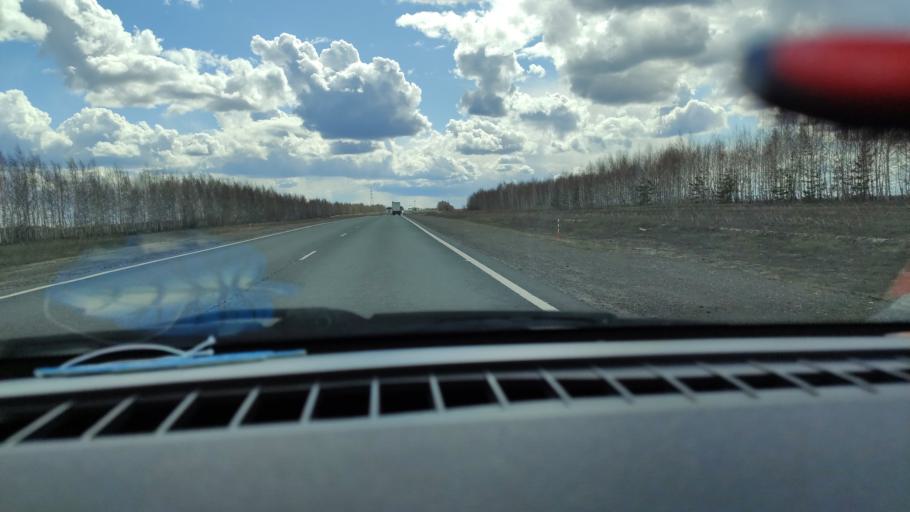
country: RU
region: Saratov
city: Dukhovnitskoye
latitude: 52.8432
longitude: 48.2498
